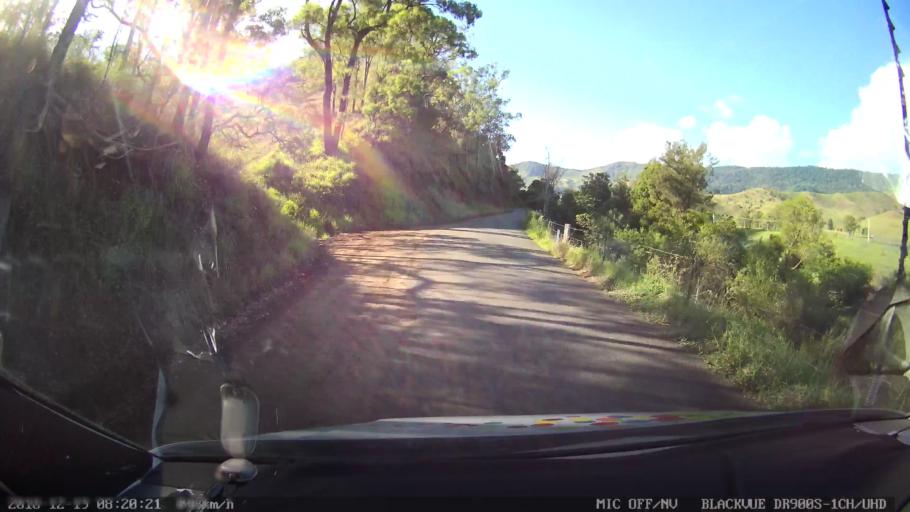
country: AU
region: New South Wales
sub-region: Kyogle
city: Kyogle
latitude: -28.2896
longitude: 152.9100
